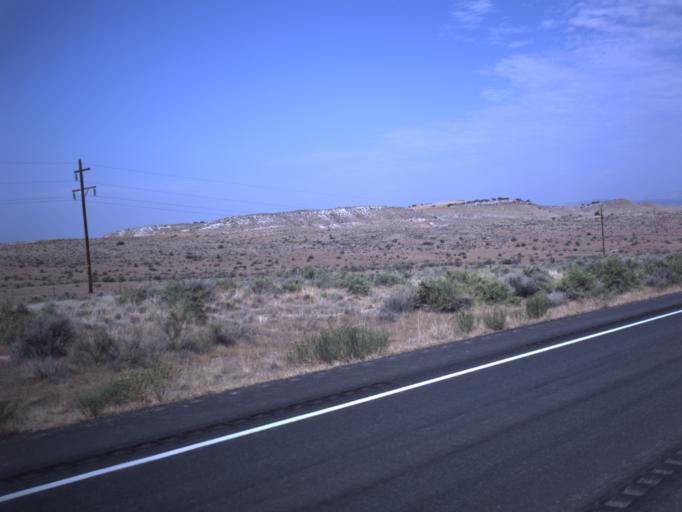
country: US
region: Utah
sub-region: Uintah County
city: Naples
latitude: 40.3351
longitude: -109.2880
